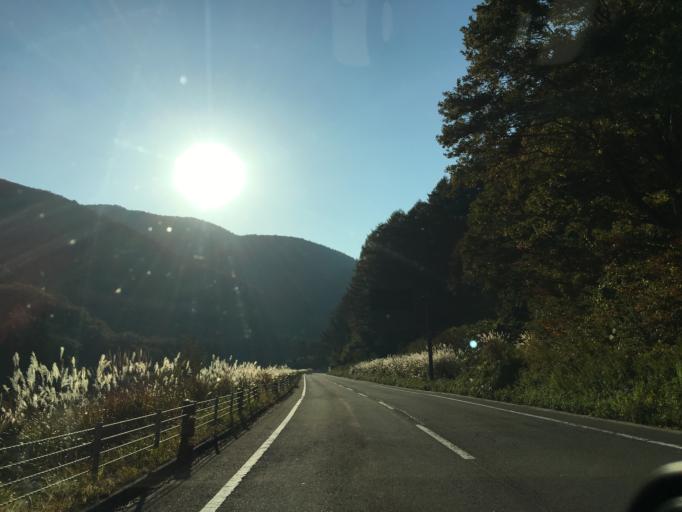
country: JP
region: Fukushima
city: Inawashiro
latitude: 37.3954
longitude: 140.1741
